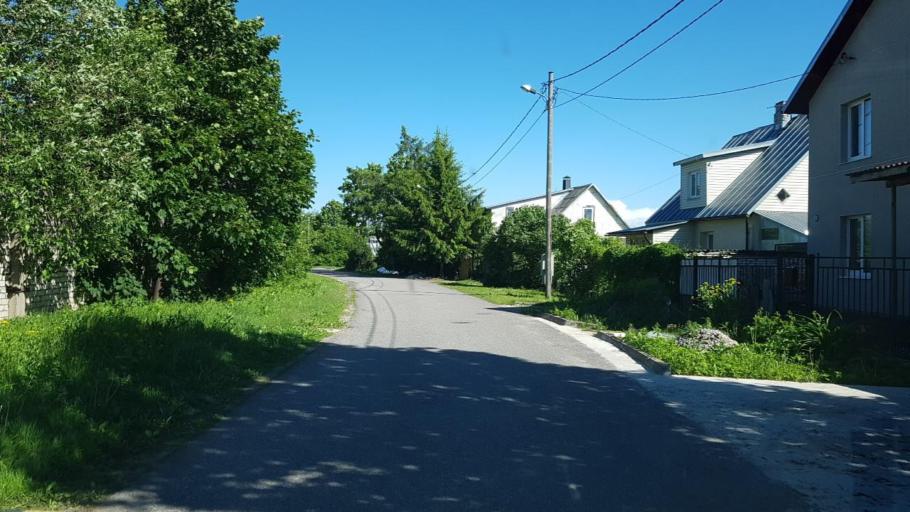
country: EE
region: Ida-Virumaa
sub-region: Narva linn
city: Narva
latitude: 59.3626
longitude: 28.1836
